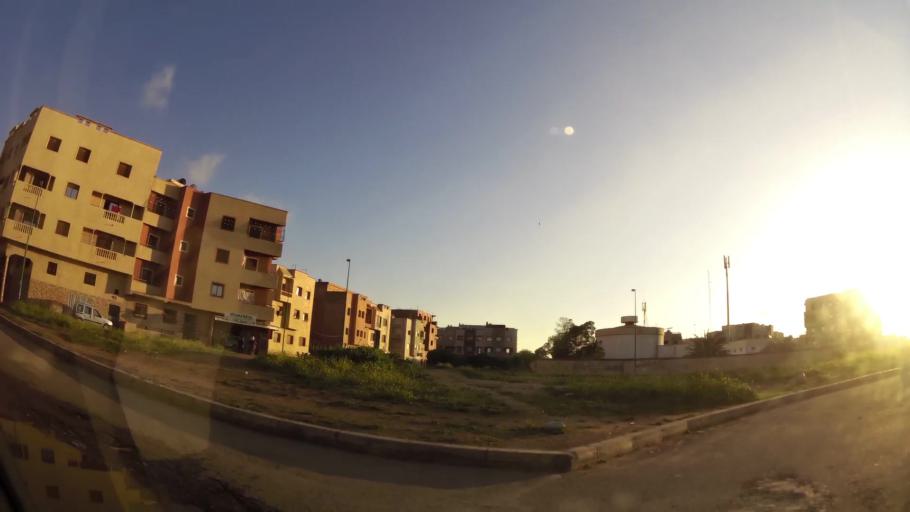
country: MA
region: Chaouia-Ouardigha
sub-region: Settat Province
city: Settat
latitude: 32.9908
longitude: -7.6009
